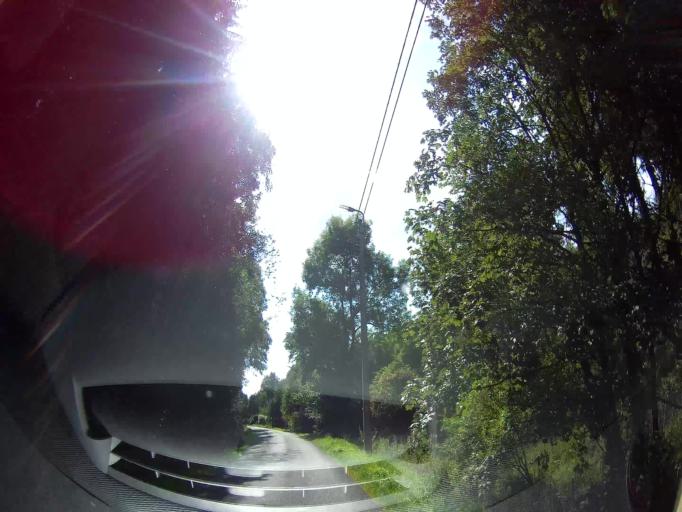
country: BE
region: Wallonia
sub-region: Province de Namur
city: Onhaye
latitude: 50.2901
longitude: 4.8003
